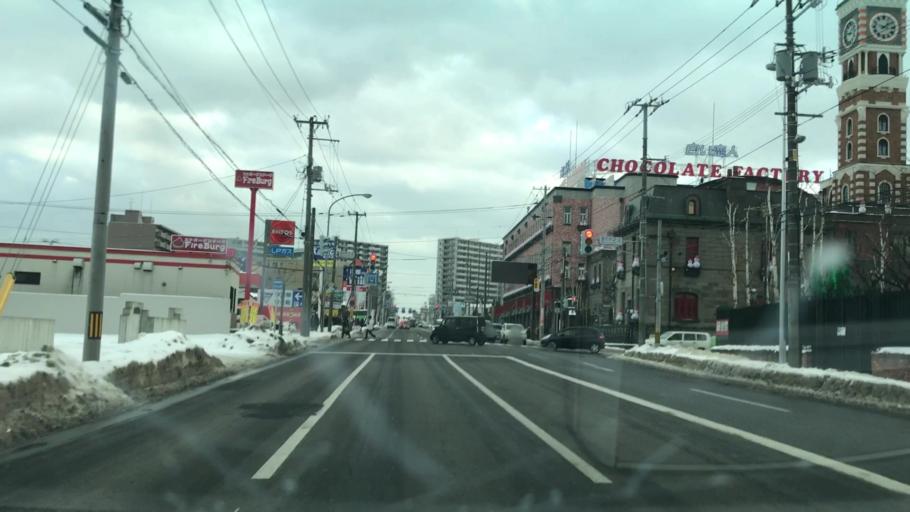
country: JP
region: Hokkaido
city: Sapporo
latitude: 43.0897
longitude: 141.2707
